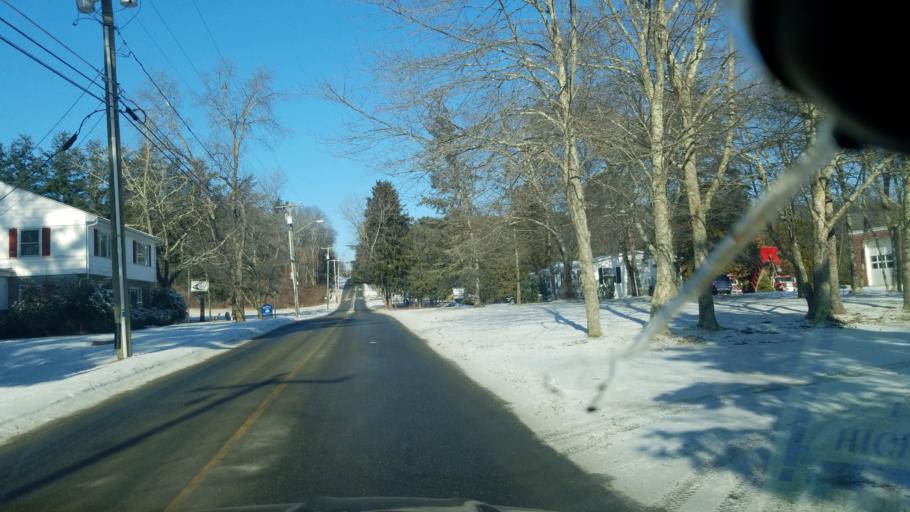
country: US
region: Connecticut
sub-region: Windham County
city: East Brooklyn
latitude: 41.8061
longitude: -71.9035
